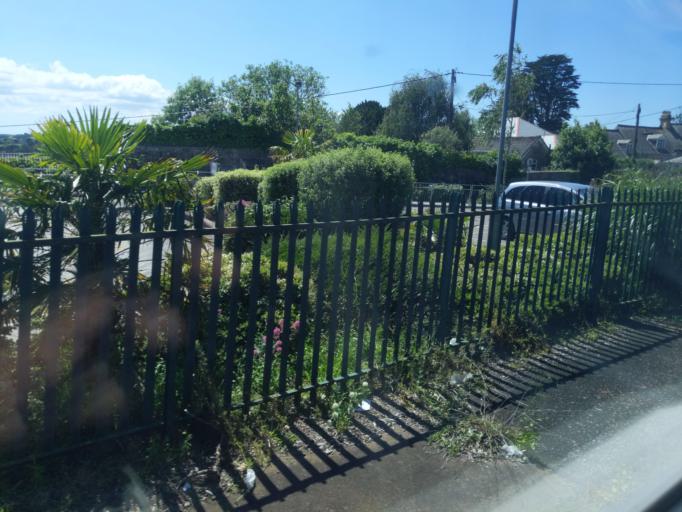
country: GB
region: England
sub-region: Cornwall
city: St Austell
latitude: 50.3397
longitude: -4.7900
